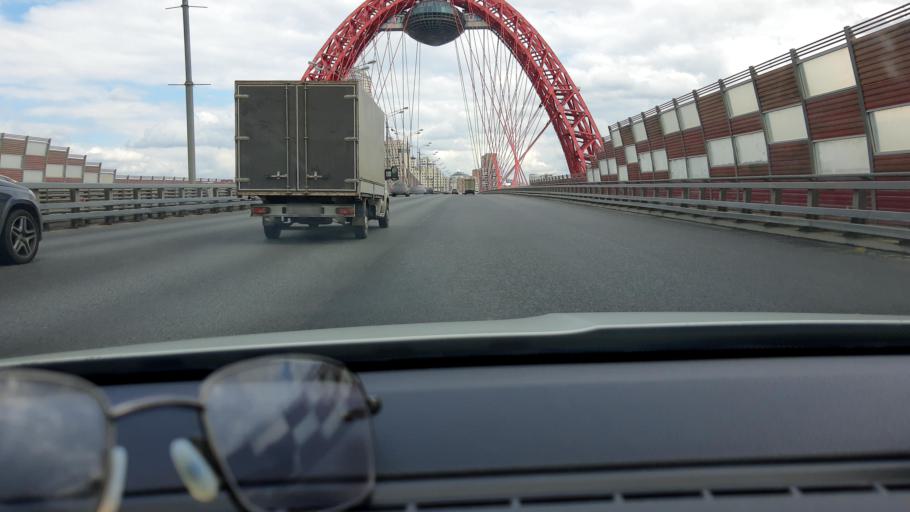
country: RU
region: Moscow
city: Shchukino
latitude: 55.7733
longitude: 37.4406
